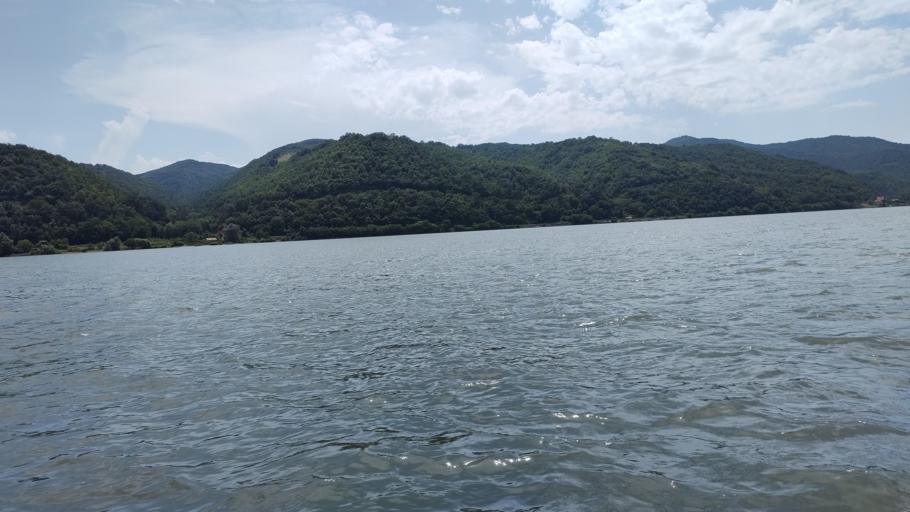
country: RO
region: Caras-Severin
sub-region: Comuna Berzasca
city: Berzasca
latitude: 44.6436
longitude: 21.9316
